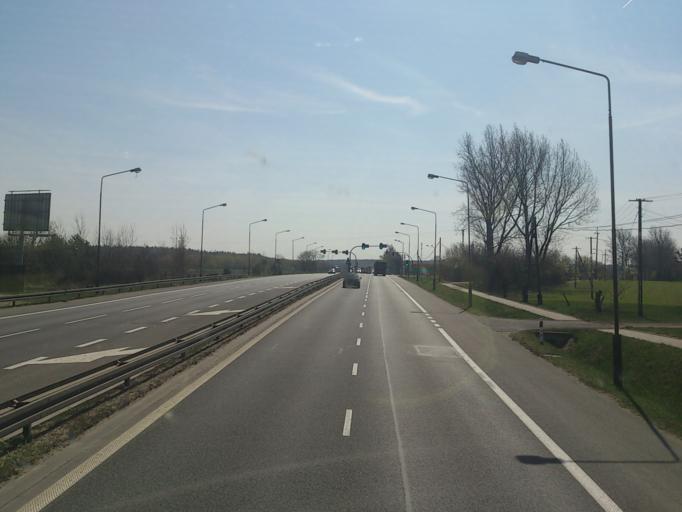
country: PL
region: Lodz Voivodeship
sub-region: Powiat lodzki wschodni
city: Tuszyn
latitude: 51.5660
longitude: 19.5850
